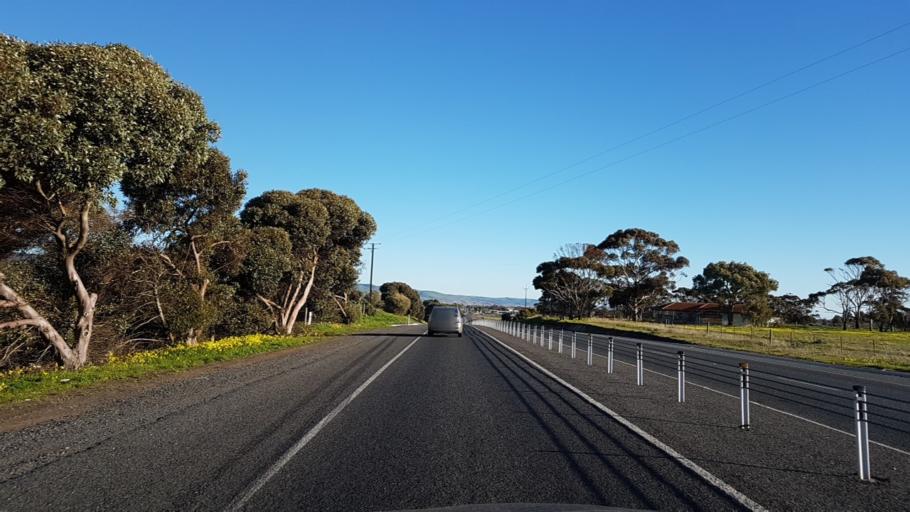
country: AU
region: South Australia
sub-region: Onkaparinga
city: Aldinga
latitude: -35.2599
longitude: 138.4906
